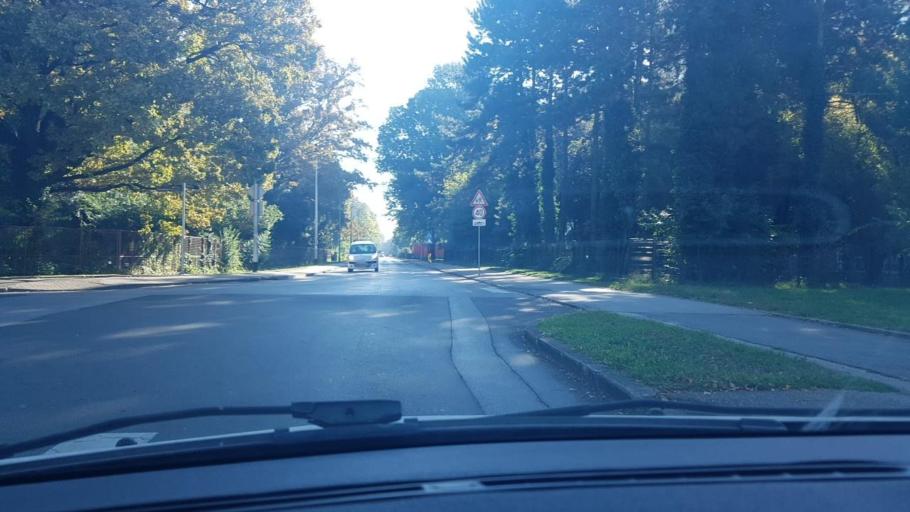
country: HR
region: Grad Zagreb
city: Novi Zagreb
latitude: 45.7735
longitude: 15.9717
